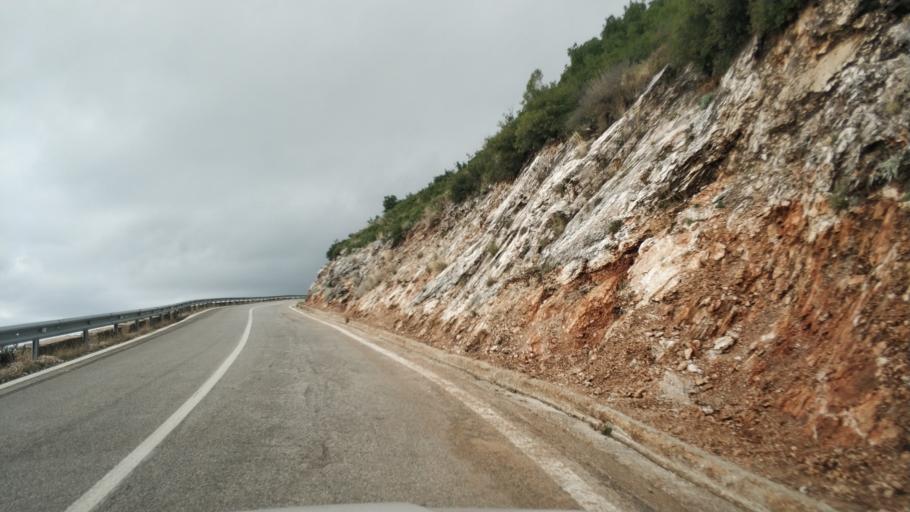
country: AL
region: Vlore
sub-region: Rrethi i Vlores
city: Vranisht
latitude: 40.1828
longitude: 19.5988
